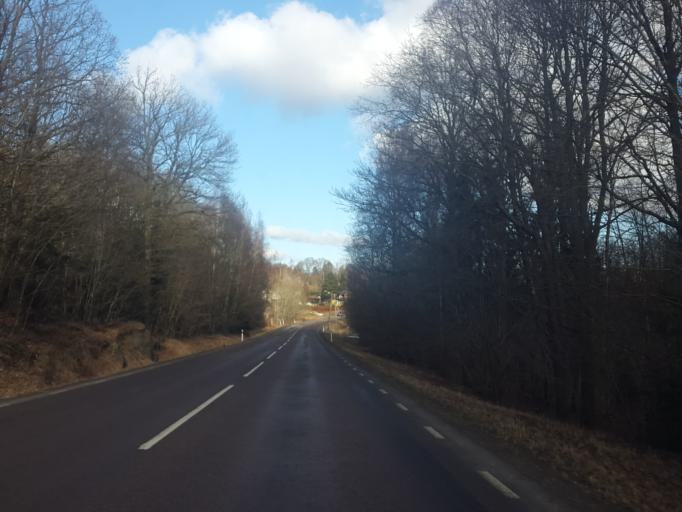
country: SE
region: Vaestra Goetaland
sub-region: Lerums Kommun
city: Grabo
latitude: 57.8664
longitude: 12.3215
